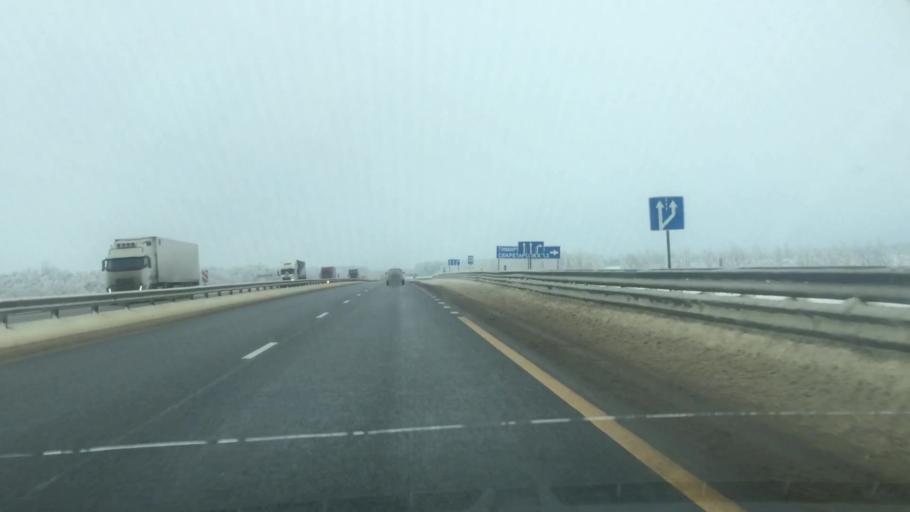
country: RU
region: Lipetsk
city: Zadonsk
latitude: 52.5038
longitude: 38.7555
